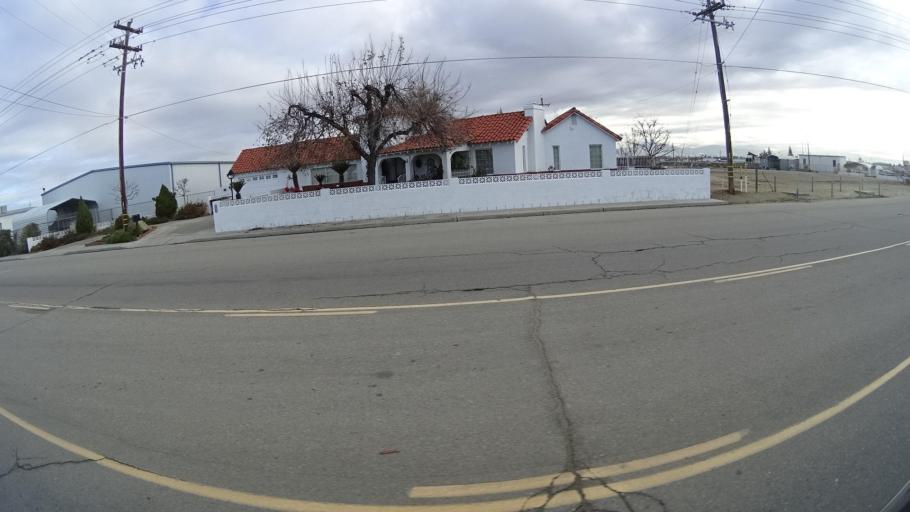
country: US
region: California
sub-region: Kern County
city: Greenacres
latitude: 35.3862
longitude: -119.0743
